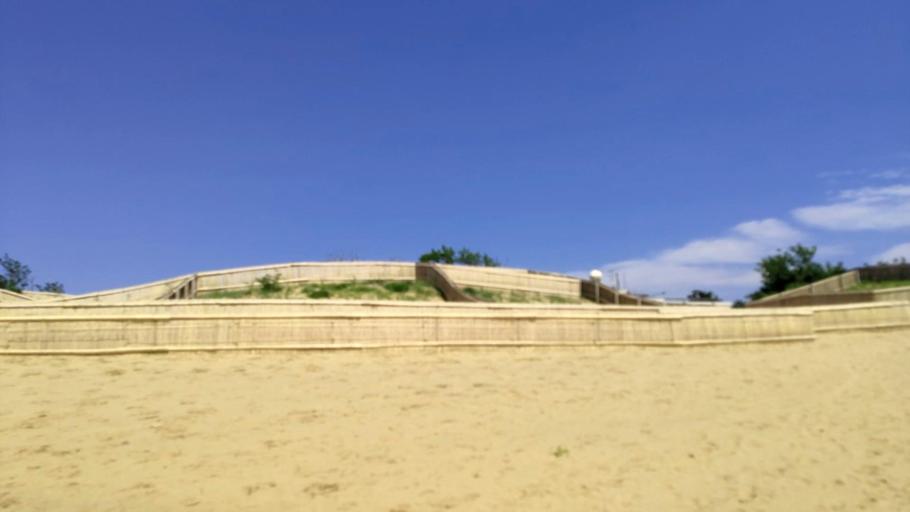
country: JP
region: Tottori
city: Tottori
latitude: 35.5419
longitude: 134.2355
